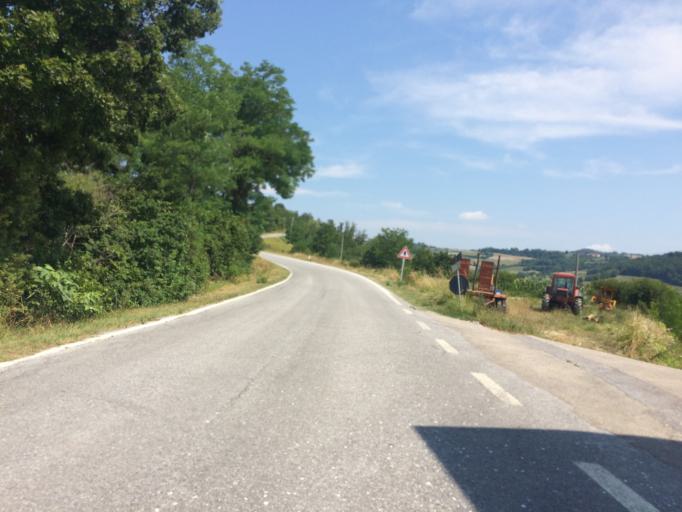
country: IT
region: Piedmont
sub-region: Provincia di Cuneo
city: Cissone
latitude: 44.5606
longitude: 8.0387
